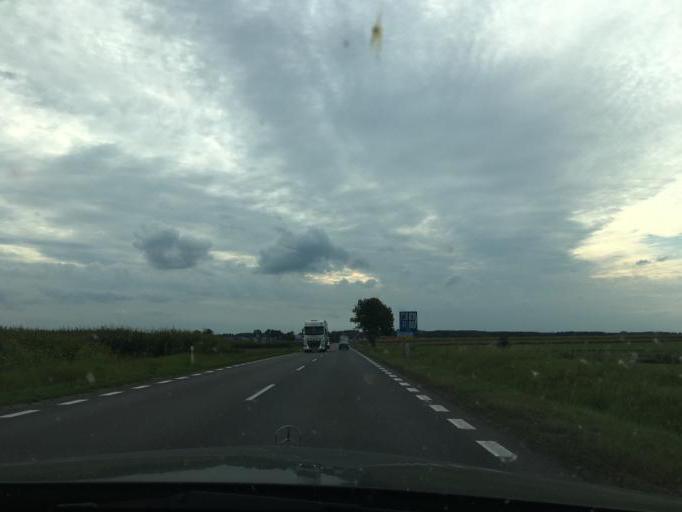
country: PL
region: Podlasie
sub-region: Powiat grajewski
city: Grajewo
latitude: 53.6320
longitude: 22.4212
